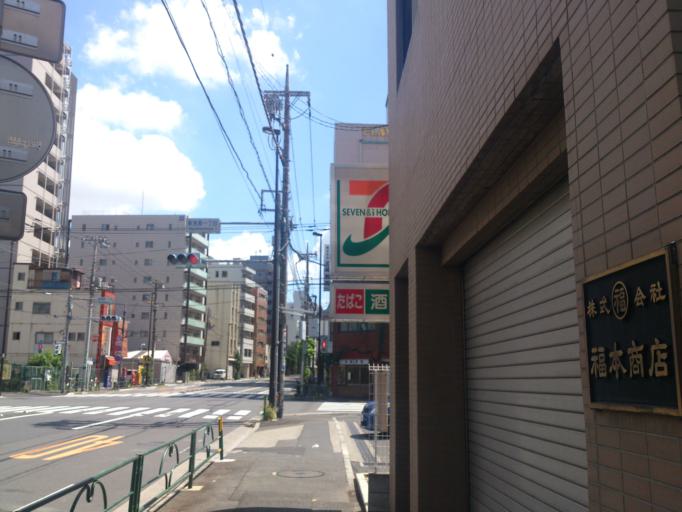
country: JP
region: Saitama
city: Soka
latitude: 35.7212
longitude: 139.8017
